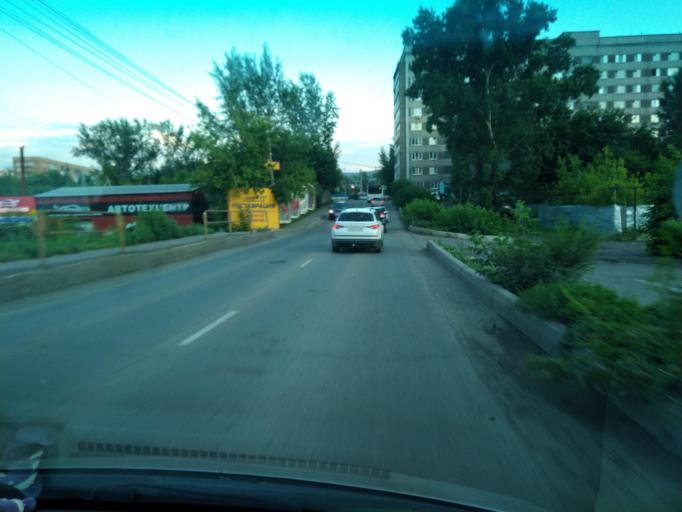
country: RU
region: Krasnoyarskiy
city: Krasnoyarsk
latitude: 55.9845
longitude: 92.8715
